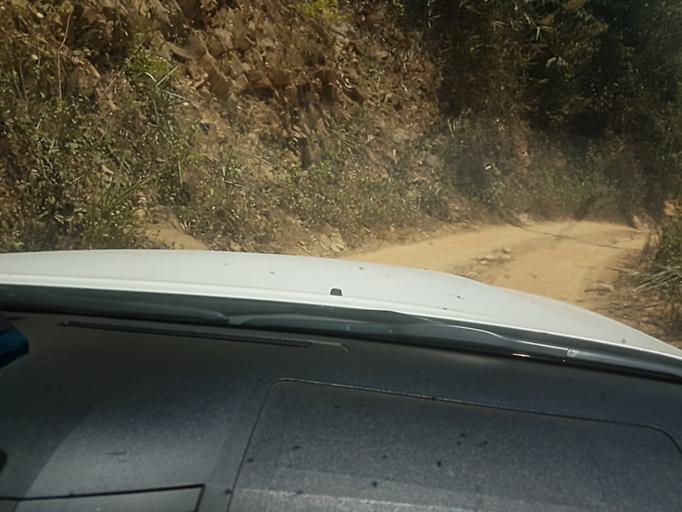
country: VN
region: Nghe An
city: Con Cuong
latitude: 18.6026
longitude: 104.7312
